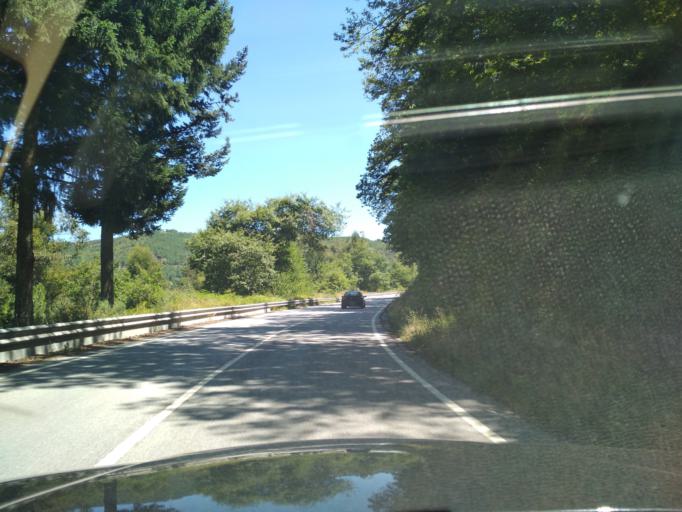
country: PT
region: Vila Real
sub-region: Ribeira de Pena
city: Ribeira de Pena
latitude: 41.5109
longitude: -7.7949
